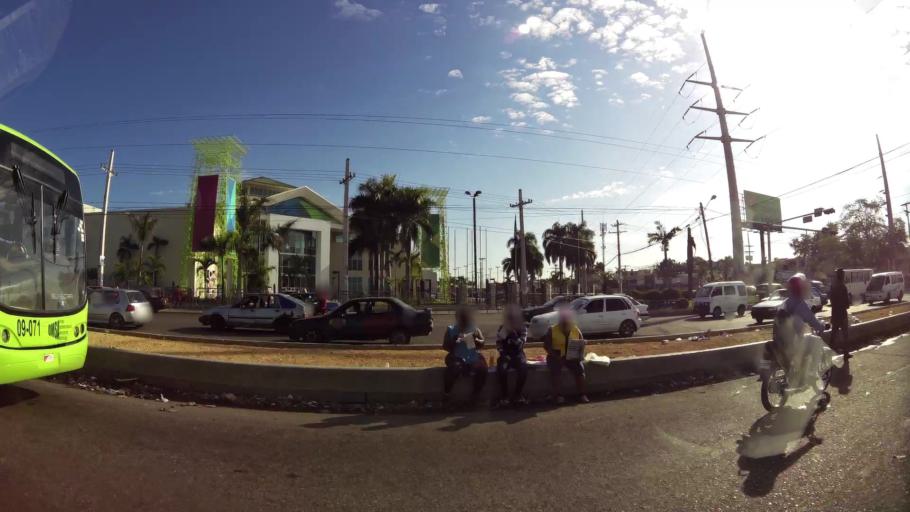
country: DO
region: Santo Domingo
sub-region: Santo Domingo
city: Santo Domingo Este
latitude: 18.5053
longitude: -69.8570
